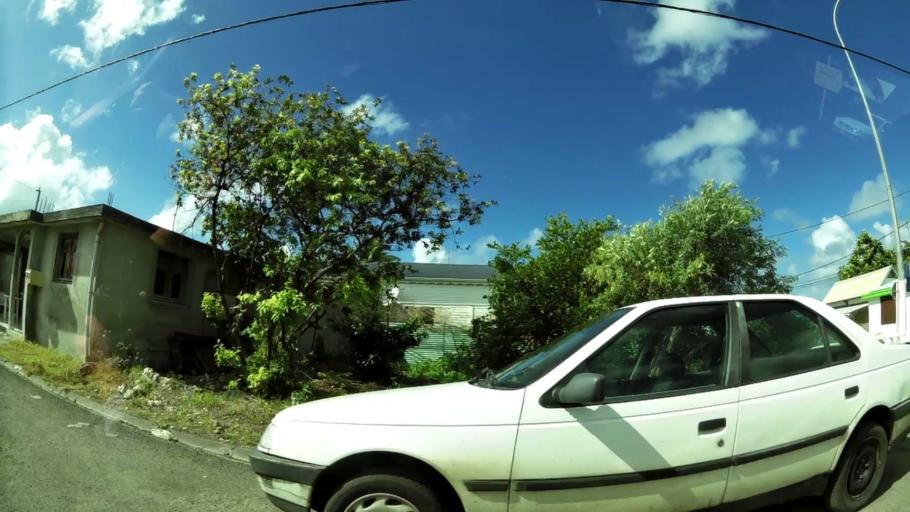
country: GP
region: Guadeloupe
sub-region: Guadeloupe
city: Port-Louis
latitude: 16.4200
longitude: -61.5297
